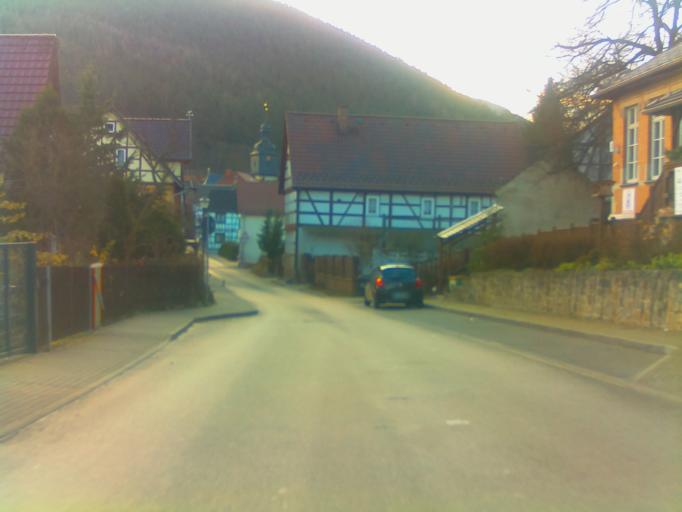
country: DE
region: Thuringia
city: Bad Blankenburg
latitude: 50.6682
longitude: 11.2914
